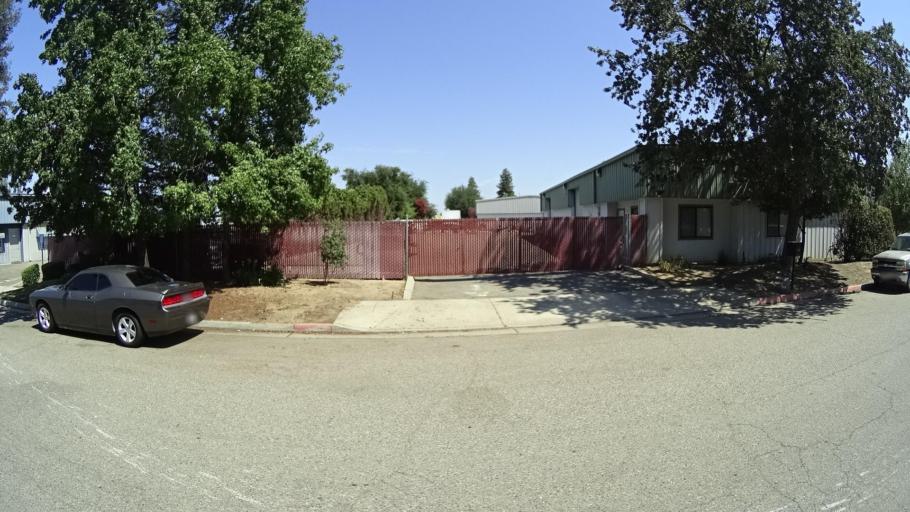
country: US
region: California
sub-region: Fresno County
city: Tarpey Village
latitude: 36.7748
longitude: -119.6904
